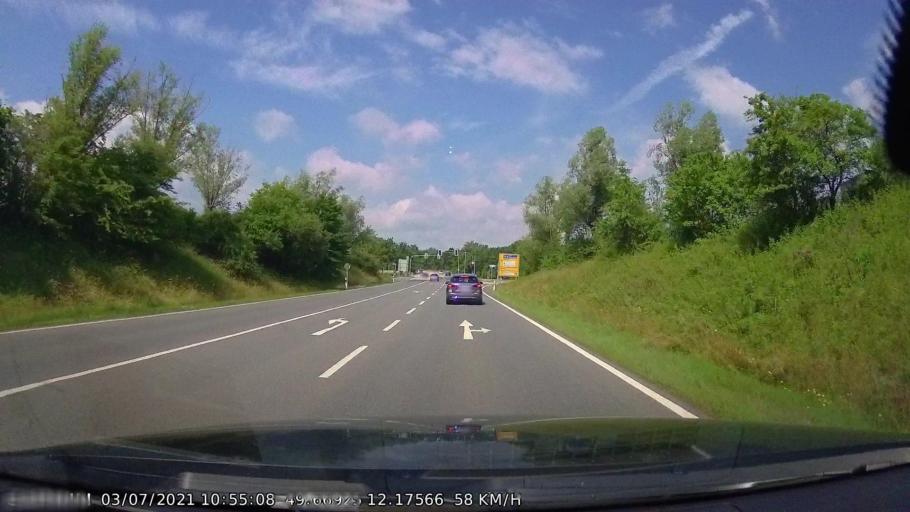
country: DE
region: Bavaria
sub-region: Upper Palatinate
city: Weiden
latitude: 49.6692
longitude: 12.1756
